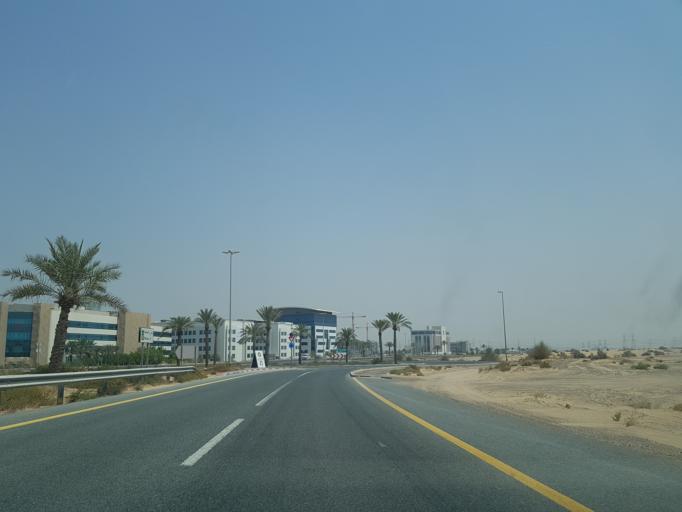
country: AE
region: Ash Shariqah
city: Sharjah
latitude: 25.1218
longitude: 55.4270
